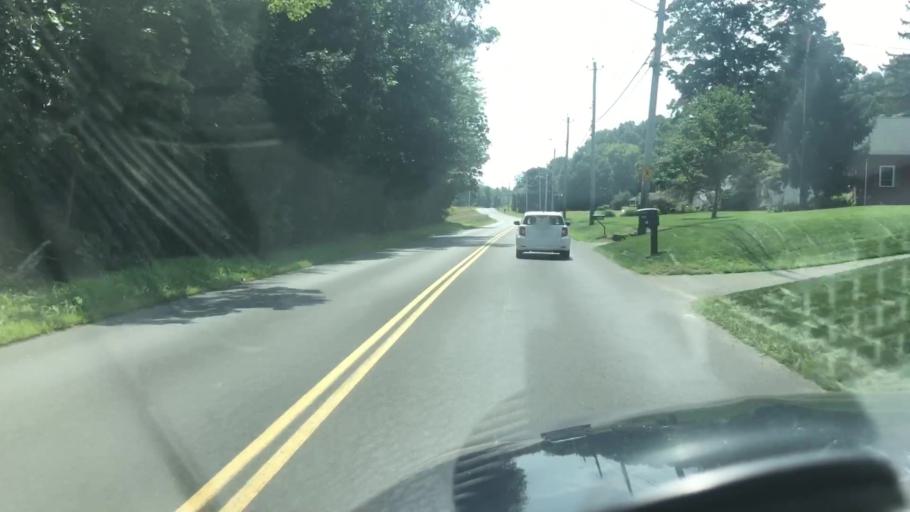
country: US
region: Massachusetts
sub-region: Hampden County
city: Westfield
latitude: 42.1288
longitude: -72.6977
